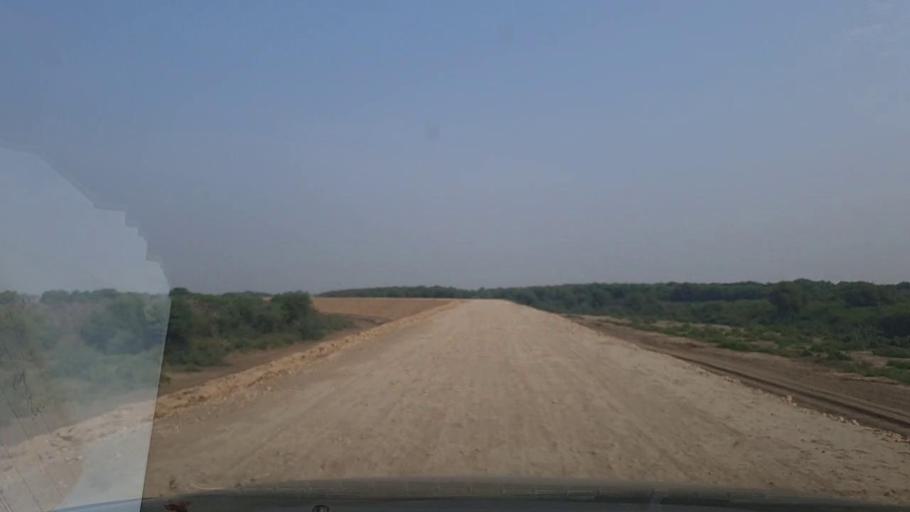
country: PK
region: Sindh
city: Bulri
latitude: 24.9703
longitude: 68.2908
